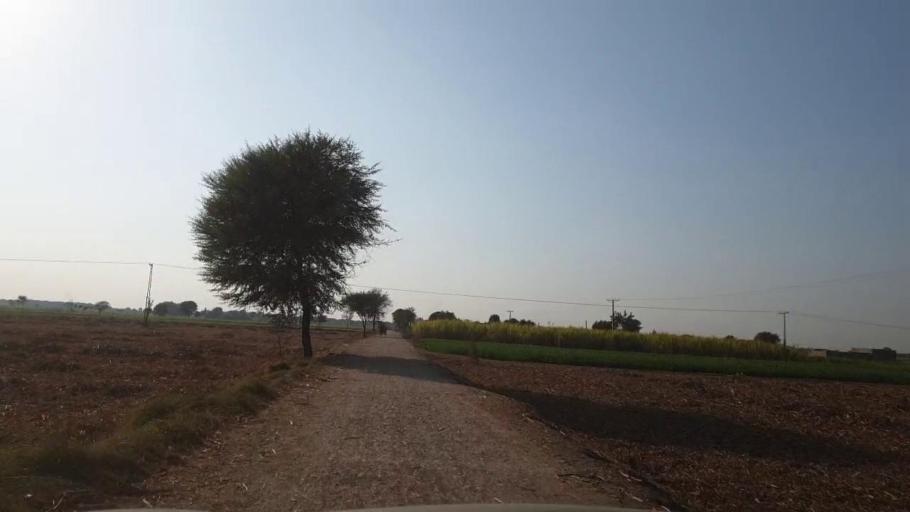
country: PK
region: Sindh
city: Tando Allahyar
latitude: 25.5762
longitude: 68.6583
